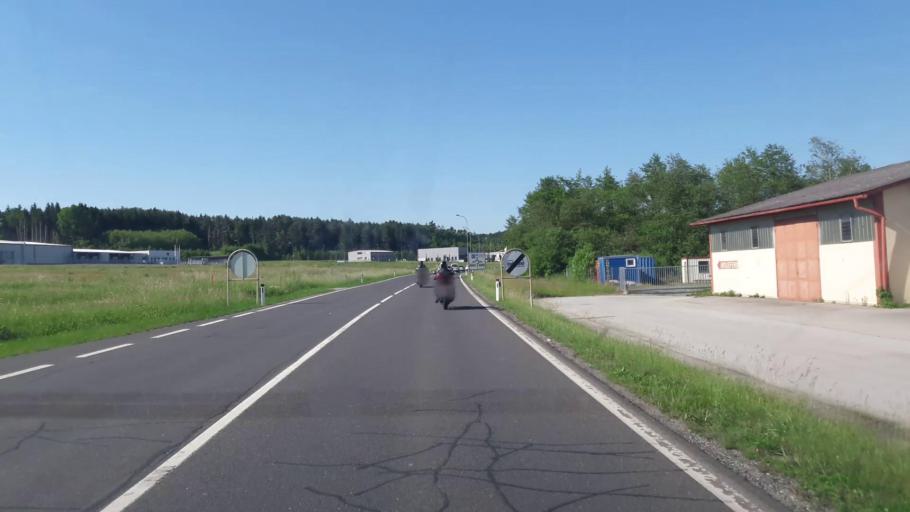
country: AT
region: Burgenland
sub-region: Politischer Bezirk Oberwart
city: Kemeten
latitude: 47.2696
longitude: 16.1526
